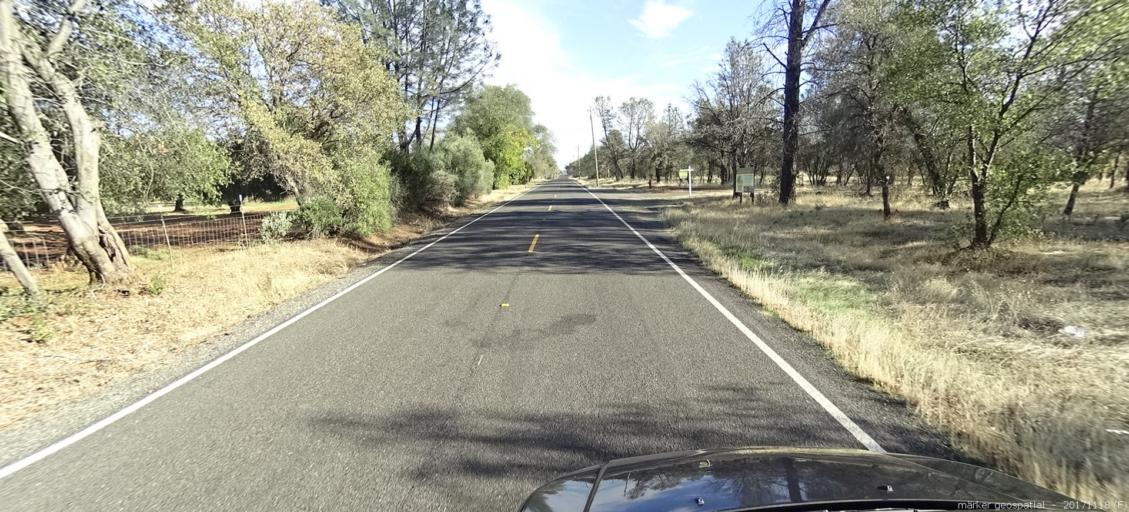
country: US
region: California
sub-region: Shasta County
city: Redding
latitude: 40.4499
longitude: -122.4504
